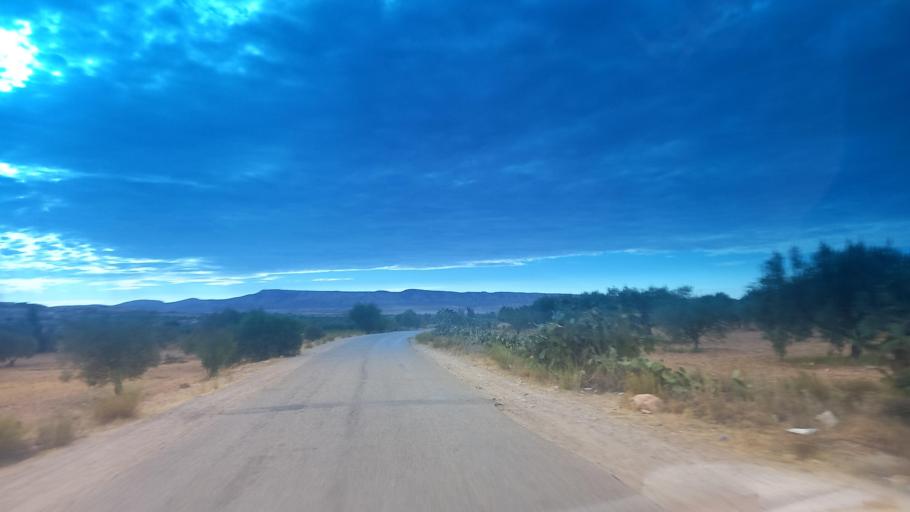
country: TN
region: Al Qasrayn
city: Sbiba
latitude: 35.3783
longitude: 9.0612
